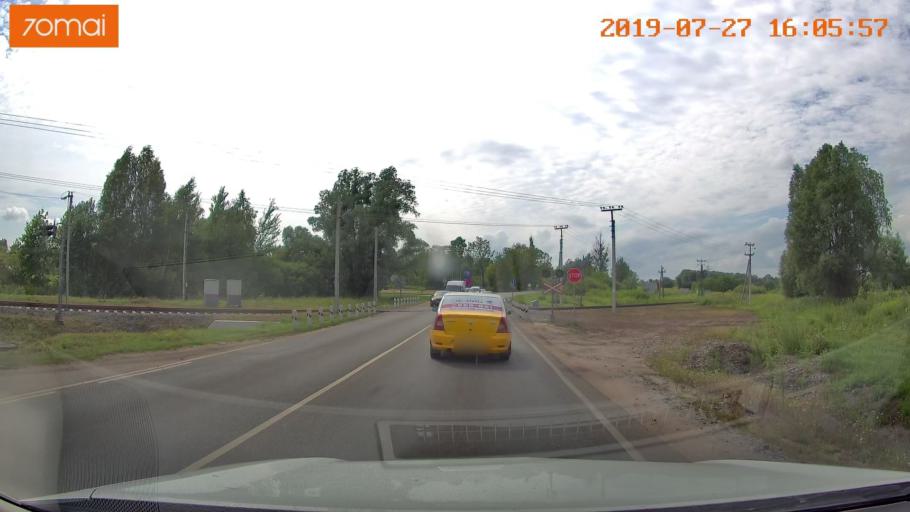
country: RU
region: Kaliningrad
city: Chernyakhovsk
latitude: 54.6340
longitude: 21.7816
